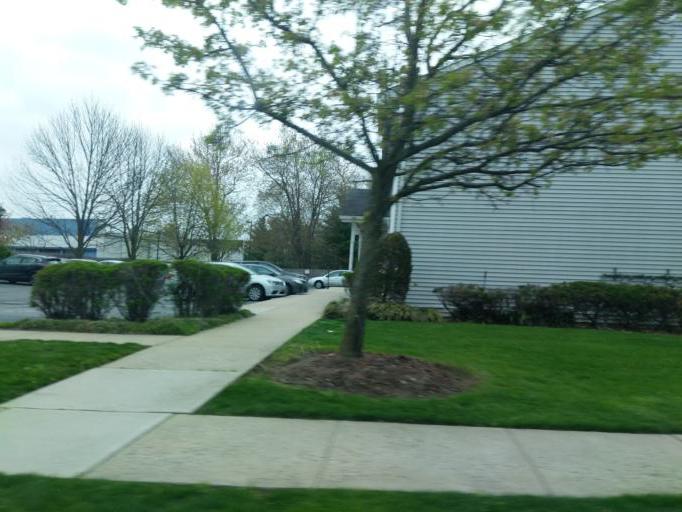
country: US
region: New York
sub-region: Nassau County
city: Baldwin
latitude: 40.6549
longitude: -73.6052
